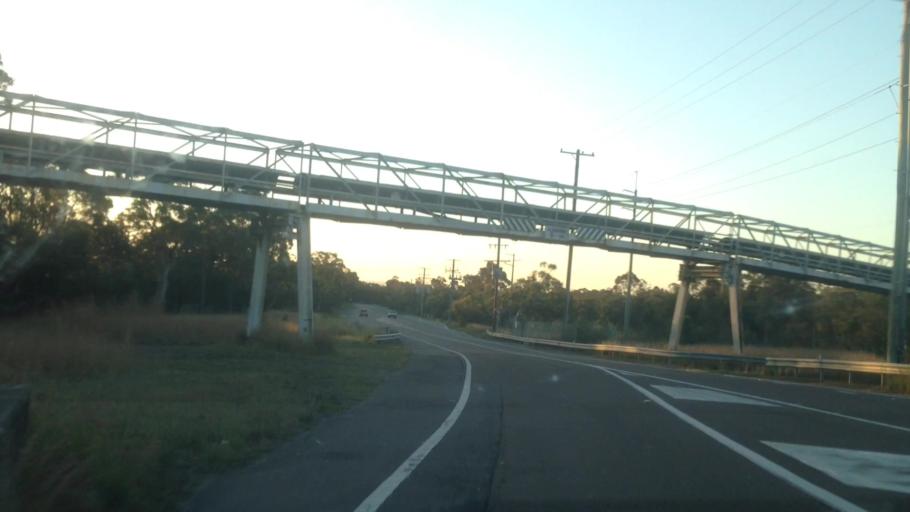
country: AU
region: New South Wales
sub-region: Wyong Shire
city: Kingfisher Shores
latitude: -33.1730
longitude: 151.5389
